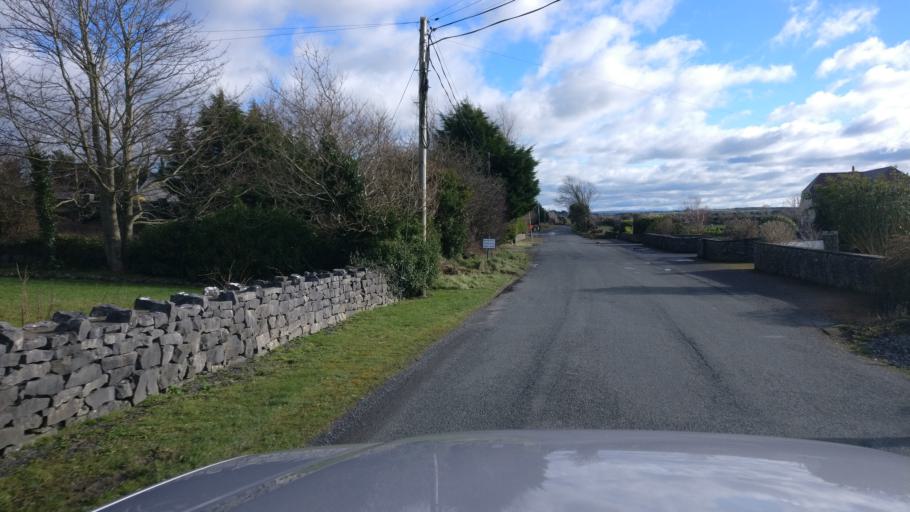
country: IE
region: Connaught
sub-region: County Galway
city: Oranmore
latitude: 53.2748
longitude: -8.8865
